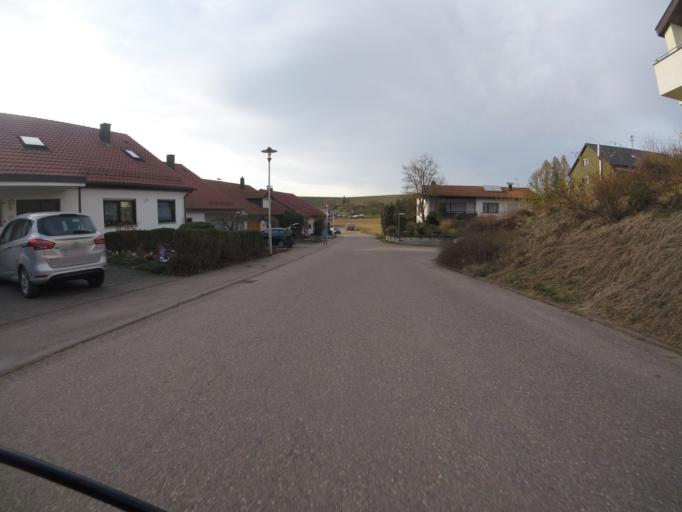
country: DE
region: Baden-Wuerttemberg
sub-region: Regierungsbezirk Stuttgart
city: Kirchberg an der Murr
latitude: 48.9624
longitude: 9.3238
